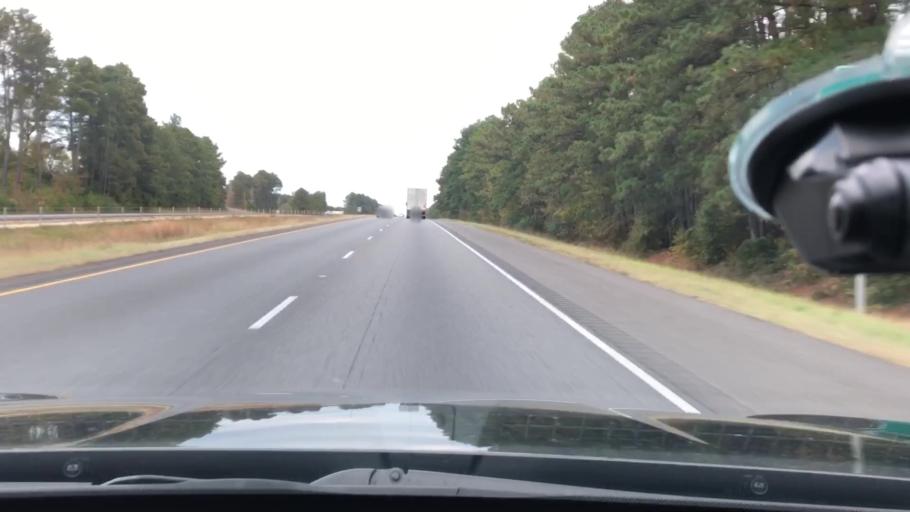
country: US
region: Arkansas
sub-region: Clark County
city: Arkadelphia
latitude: 34.2214
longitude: -93.0212
